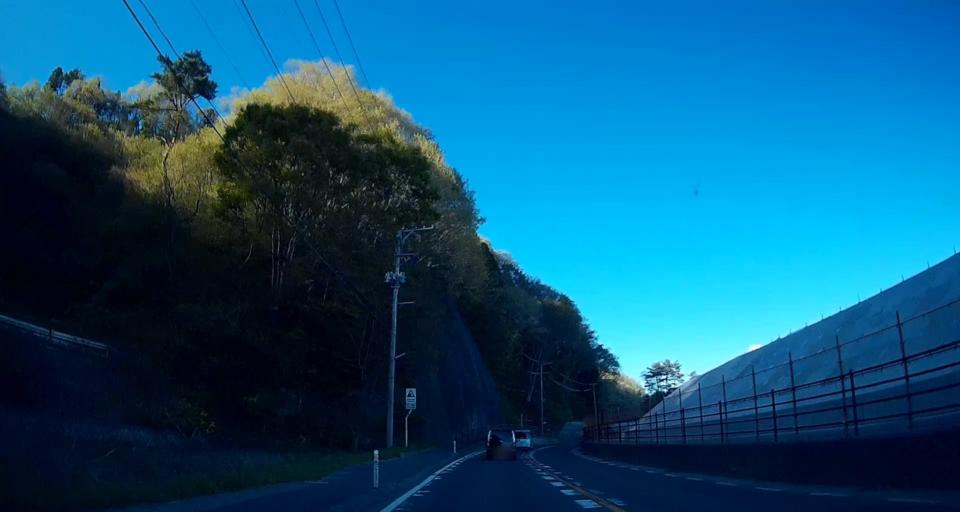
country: JP
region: Iwate
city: Miyako
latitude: 39.6095
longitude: 141.9595
